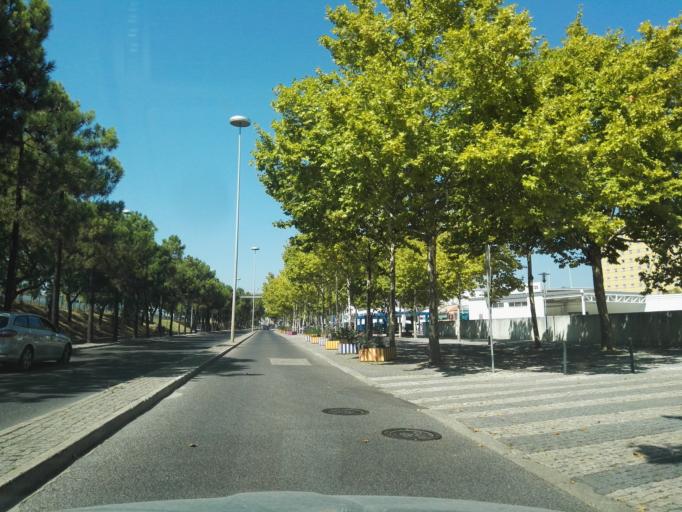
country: PT
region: Lisbon
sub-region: Loures
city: Moscavide
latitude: 38.7830
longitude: -9.0998
